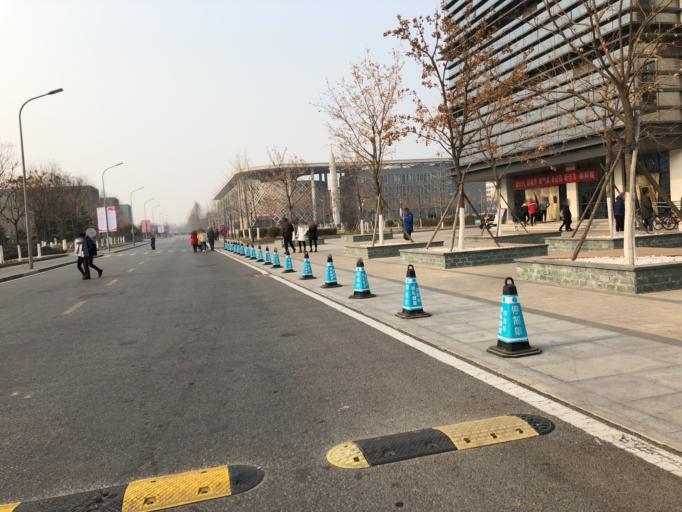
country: CN
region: Beijing
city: Daxing
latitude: 39.7469
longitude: 116.2823
